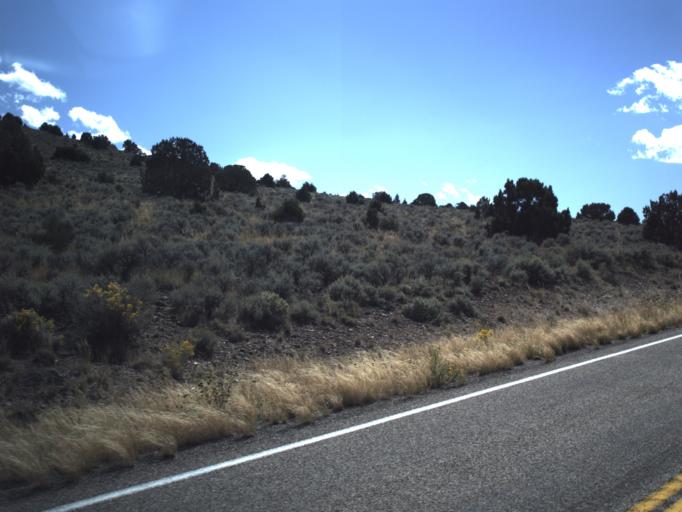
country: US
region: Utah
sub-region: Beaver County
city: Milford
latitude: 38.1184
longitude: -112.9517
